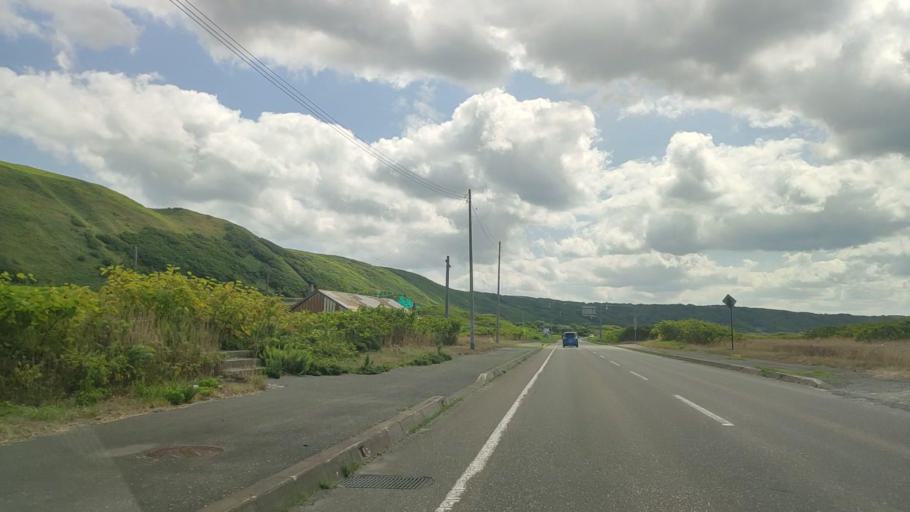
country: JP
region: Hokkaido
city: Wakkanai
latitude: 45.3077
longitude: 141.6200
